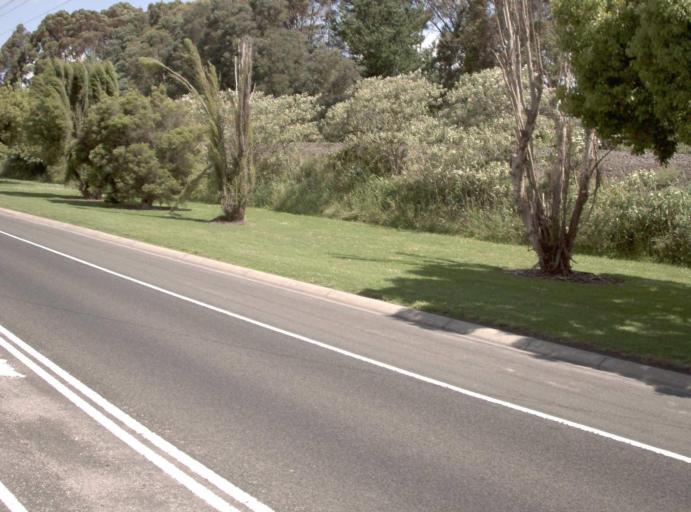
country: AU
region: Victoria
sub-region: Latrobe
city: Moe
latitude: -38.1812
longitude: 146.2737
